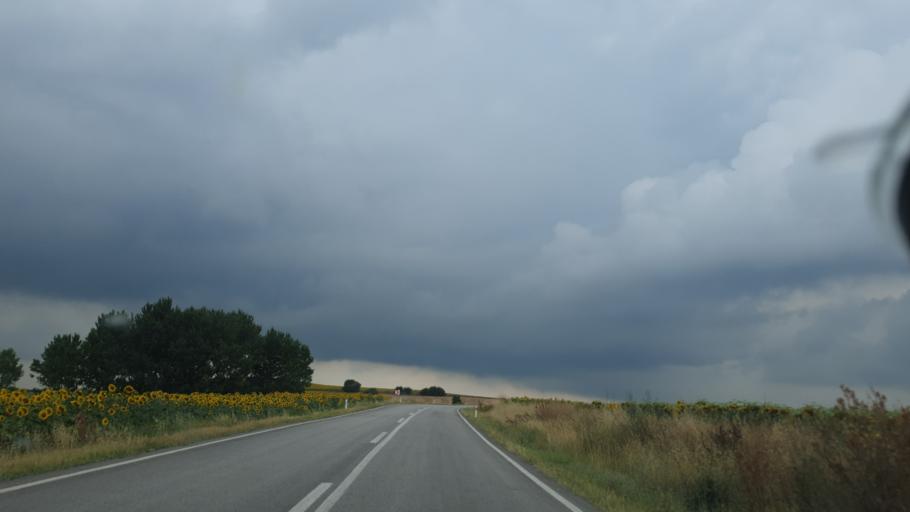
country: TR
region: Tekirdag
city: Hayrabolu
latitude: 41.2208
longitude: 26.9970
